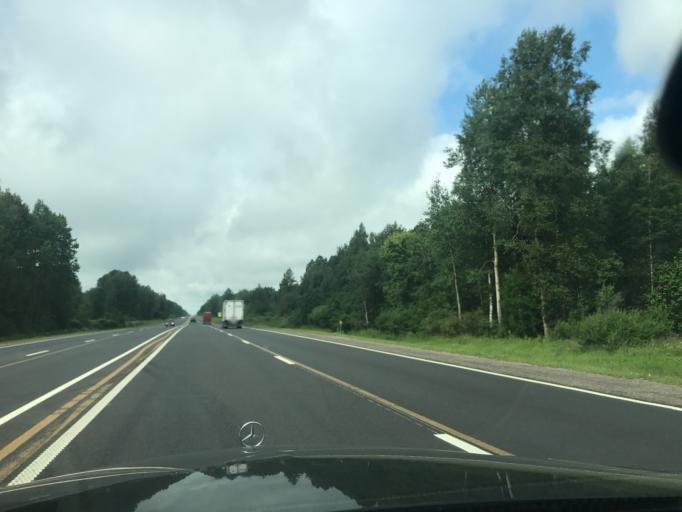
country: RU
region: Smolensk
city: Katyn'
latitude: 54.7828
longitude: 31.5619
